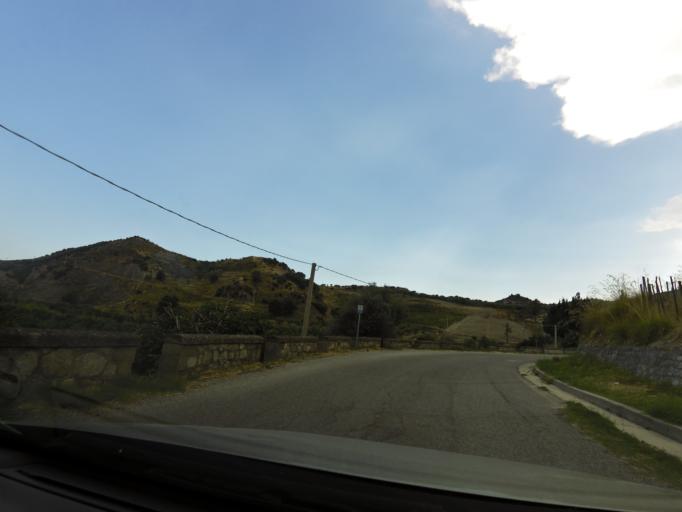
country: IT
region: Calabria
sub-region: Provincia di Reggio Calabria
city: Stilo
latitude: 38.4626
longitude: 16.4952
